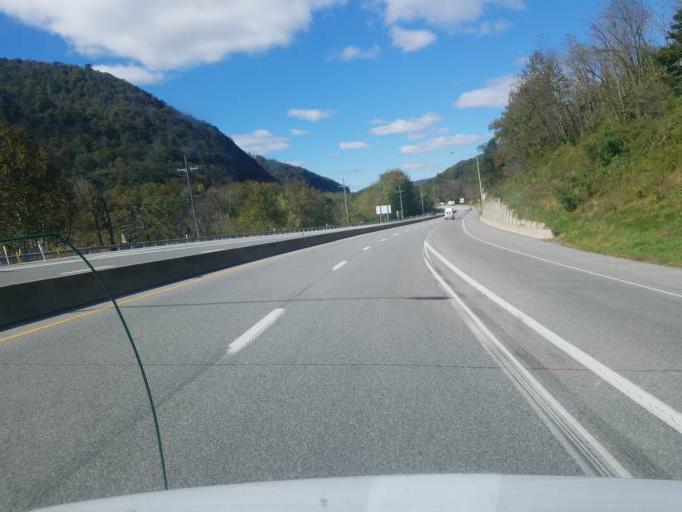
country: US
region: Pennsylvania
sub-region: Bedford County
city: Everett
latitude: 40.0100
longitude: -78.3851
